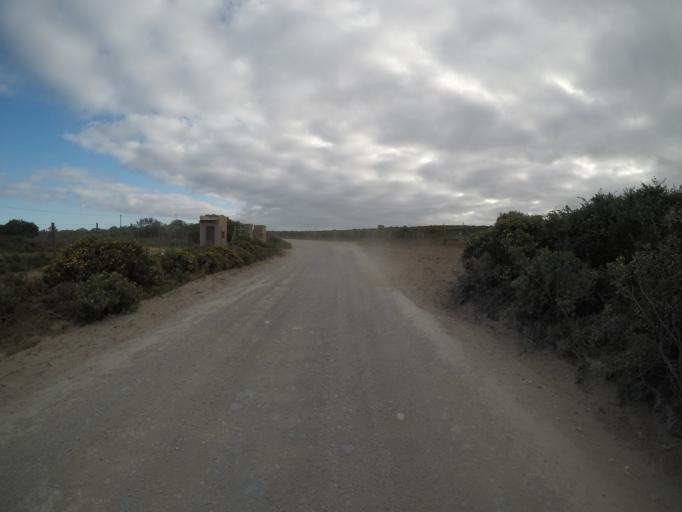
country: ZA
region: Western Cape
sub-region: Eden District Municipality
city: Riversdale
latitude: -34.4196
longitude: 21.3364
